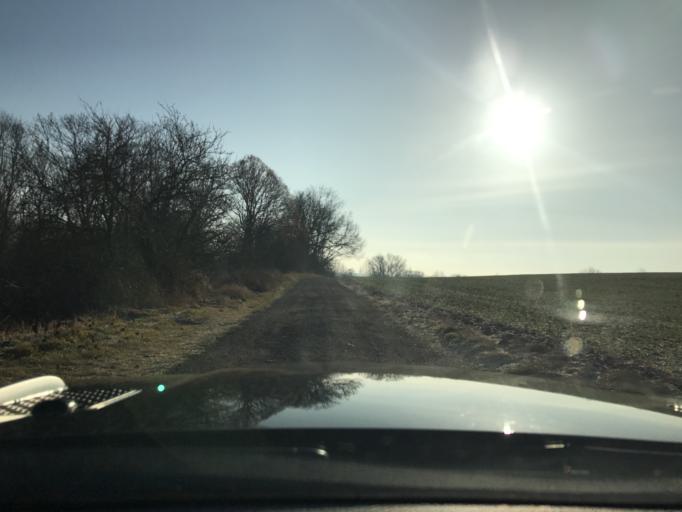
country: DE
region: Thuringia
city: Muehlhausen
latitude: 51.2375
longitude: 10.4454
